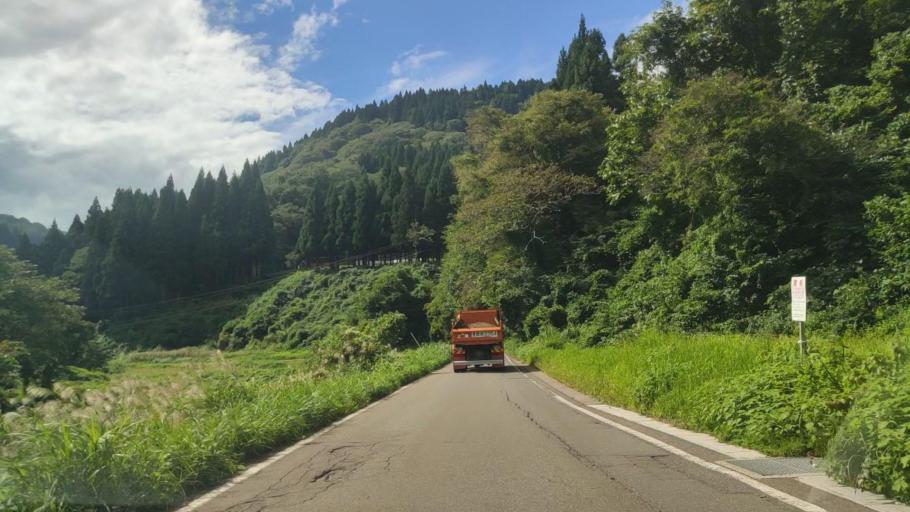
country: JP
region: Niigata
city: Arai
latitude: 36.9440
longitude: 138.2915
